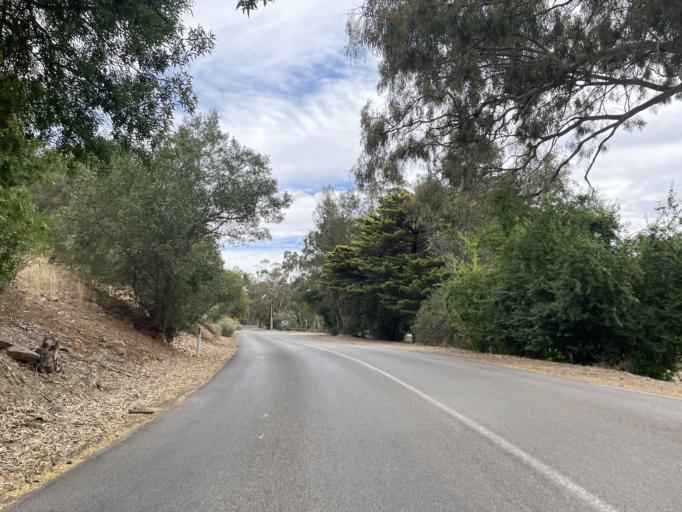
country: AU
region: South Australia
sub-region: Clare and Gilbert Valleys
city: Clare
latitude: -33.8414
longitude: 138.6132
